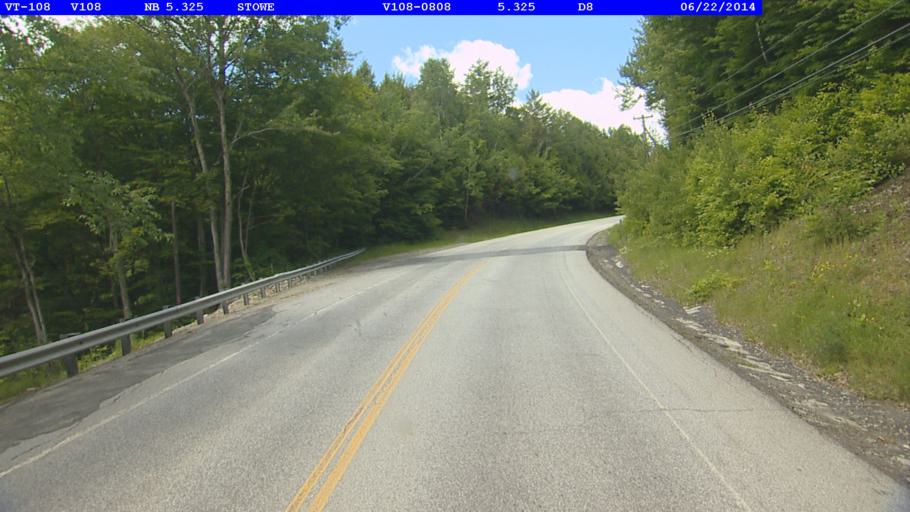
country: US
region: Vermont
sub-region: Lamoille County
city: Morristown
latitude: 44.5033
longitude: -72.7605
